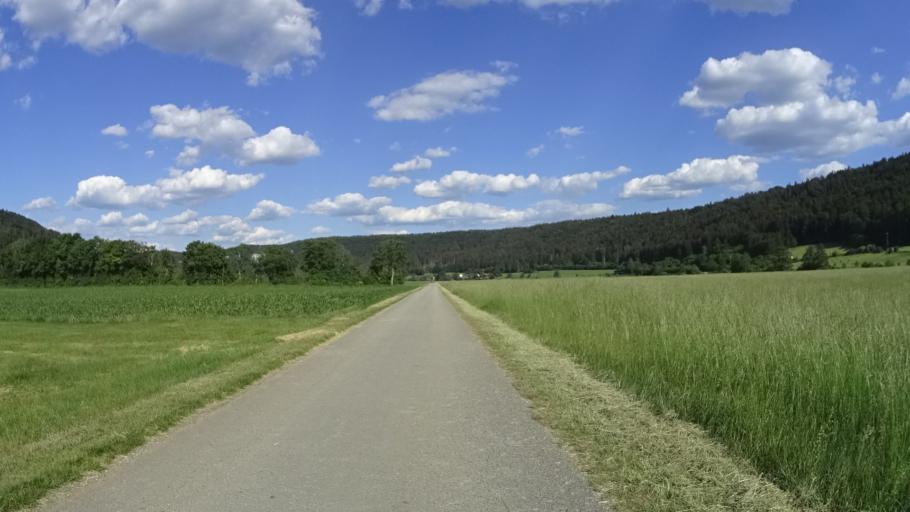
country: DE
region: Bavaria
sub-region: Upper Palatinate
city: Dietfurt
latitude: 49.0134
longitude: 11.5326
